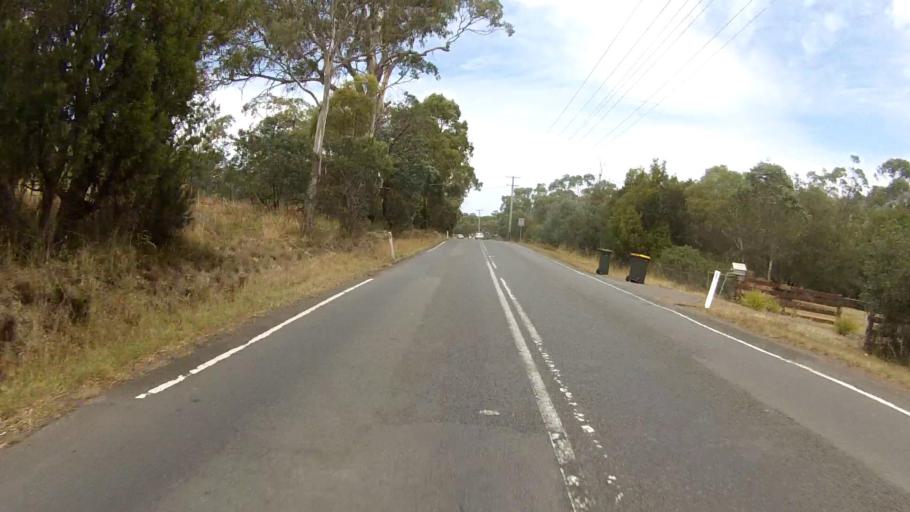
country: AU
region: Tasmania
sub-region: Clarence
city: Acton Park
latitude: -42.8717
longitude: 147.4832
